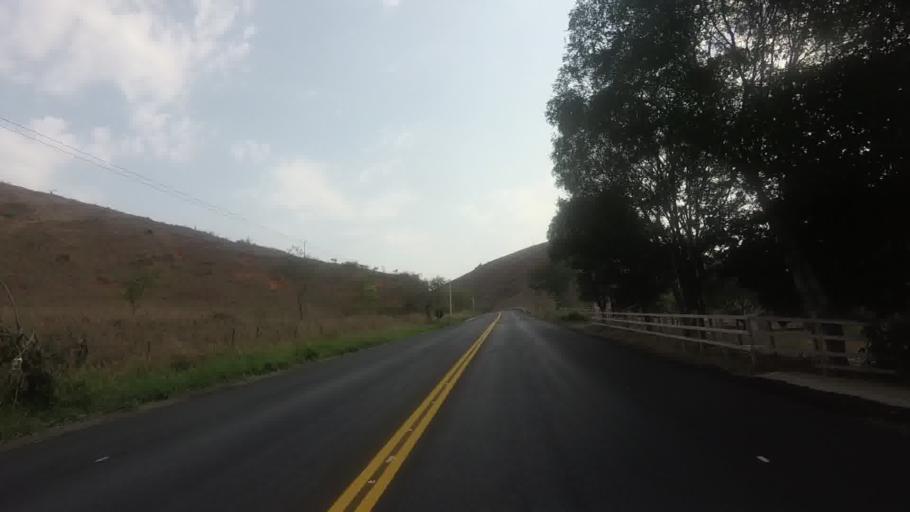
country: BR
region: Rio de Janeiro
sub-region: Bom Jesus Do Itabapoana
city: Bom Jesus do Itabapoana
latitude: -21.2418
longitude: -41.7552
